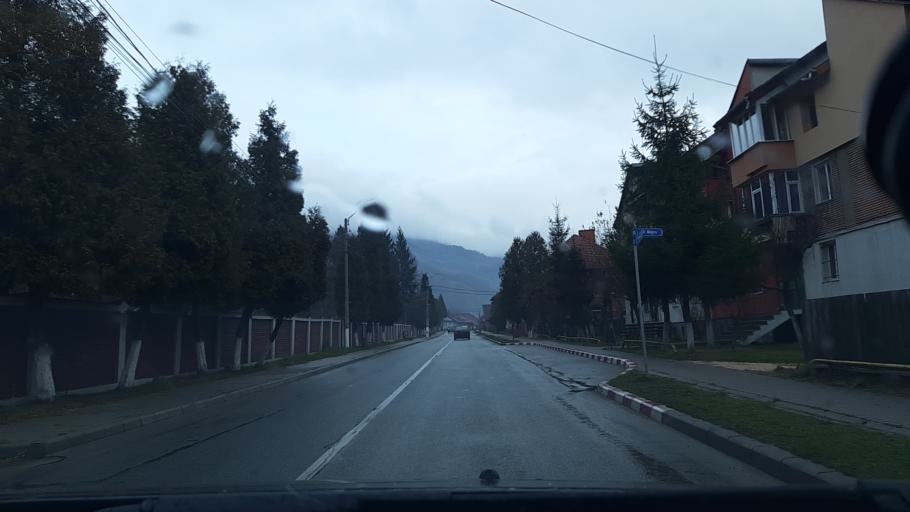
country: RO
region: Hunedoara
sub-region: Municipiul Petrosani
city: Petrosani
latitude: 45.4386
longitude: 23.3684
